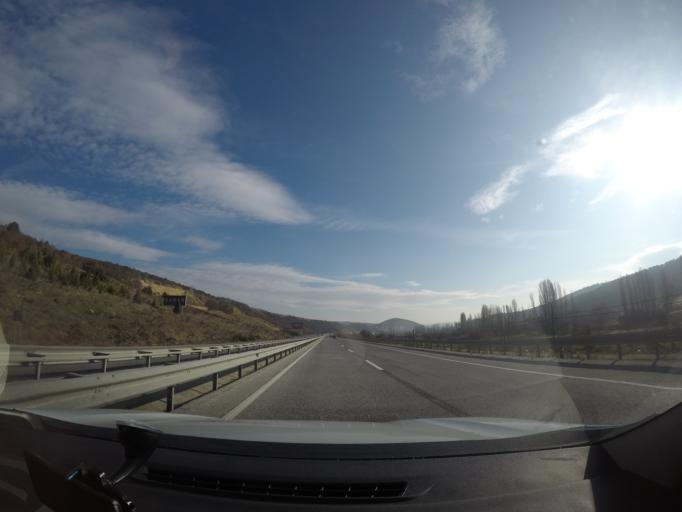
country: TR
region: Bilecik
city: Dodurga
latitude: 39.8908
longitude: 29.9433
